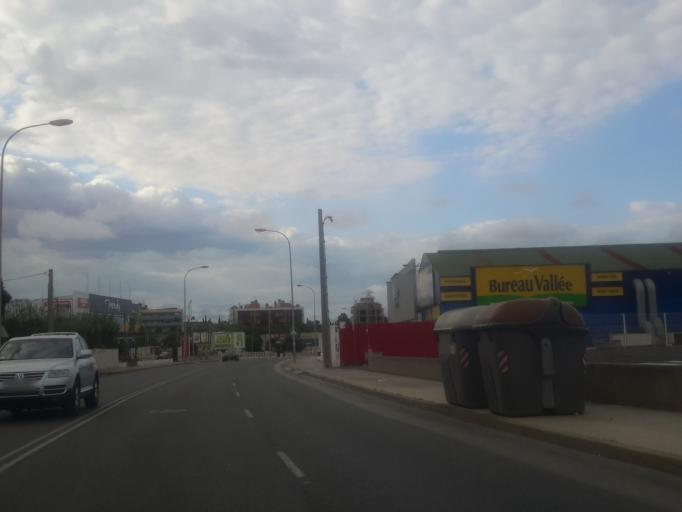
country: ES
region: Catalonia
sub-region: Provincia de Barcelona
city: Vilanova i la Geltru
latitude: 41.2287
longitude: 1.7391
